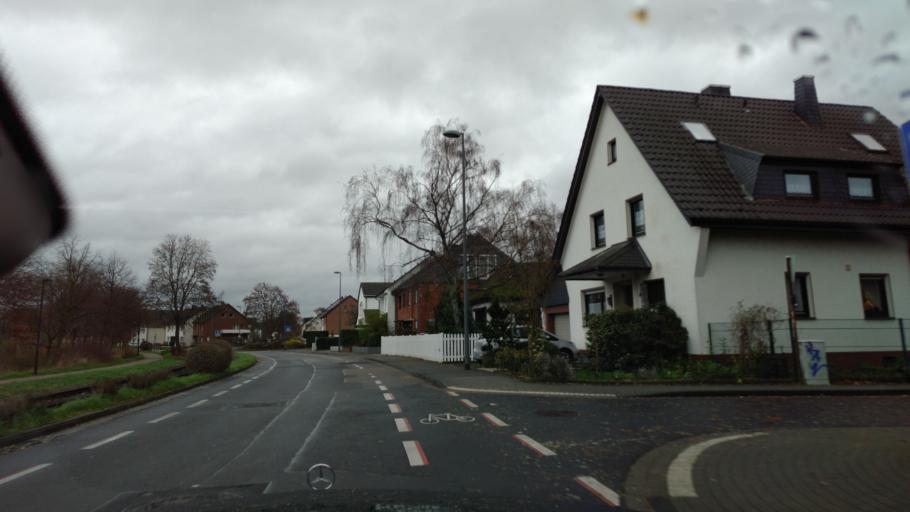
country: DE
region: North Rhine-Westphalia
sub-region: Regierungsbezirk Koln
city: Bonn
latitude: 50.7767
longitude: 7.0979
